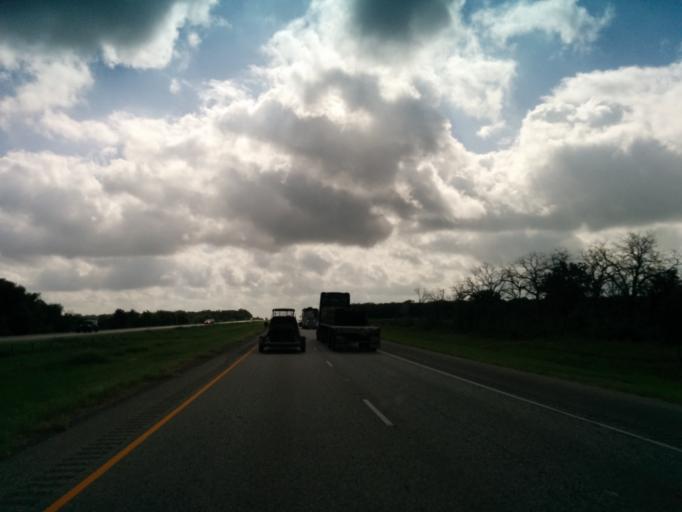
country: US
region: Texas
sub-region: Gonzales County
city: Waelder
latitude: 29.6594
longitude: -97.4052
